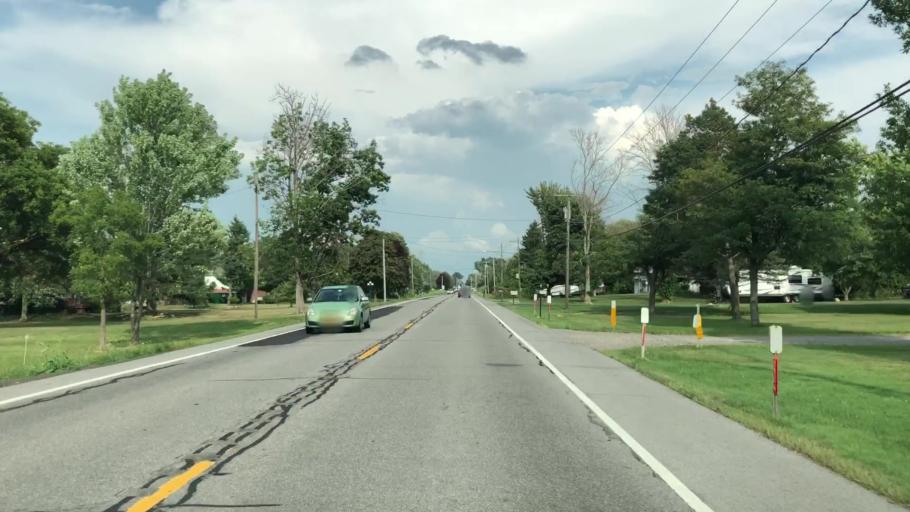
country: US
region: New York
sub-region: Erie County
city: Elma Center
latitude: 42.8555
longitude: -78.6505
